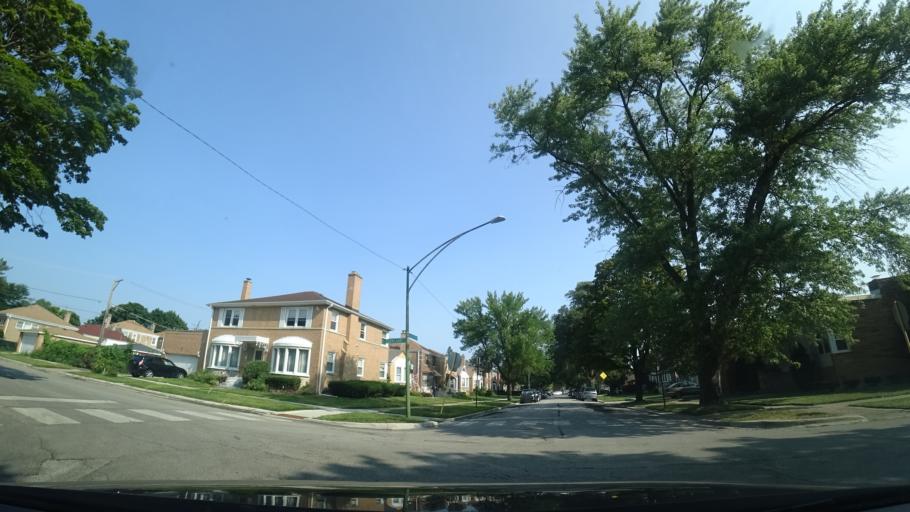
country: US
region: Illinois
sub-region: Cook County
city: Lincolnwood
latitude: 41.9920
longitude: -87.7128
